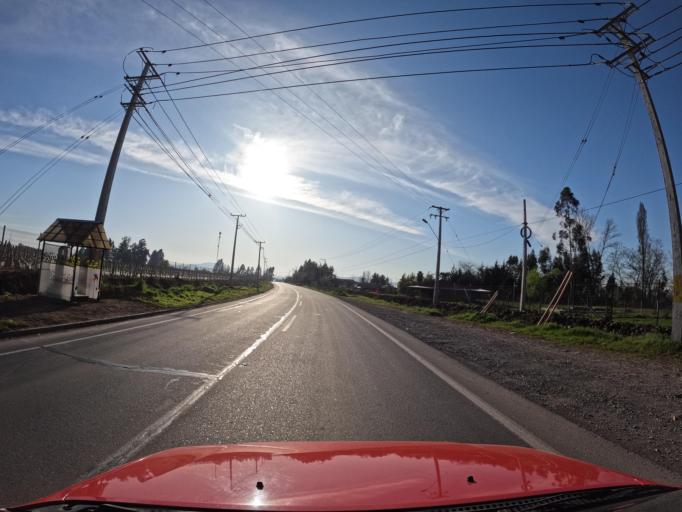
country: CL
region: Maule
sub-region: Provincia de Curico
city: Teno
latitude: -34.8591
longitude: -71.0973
